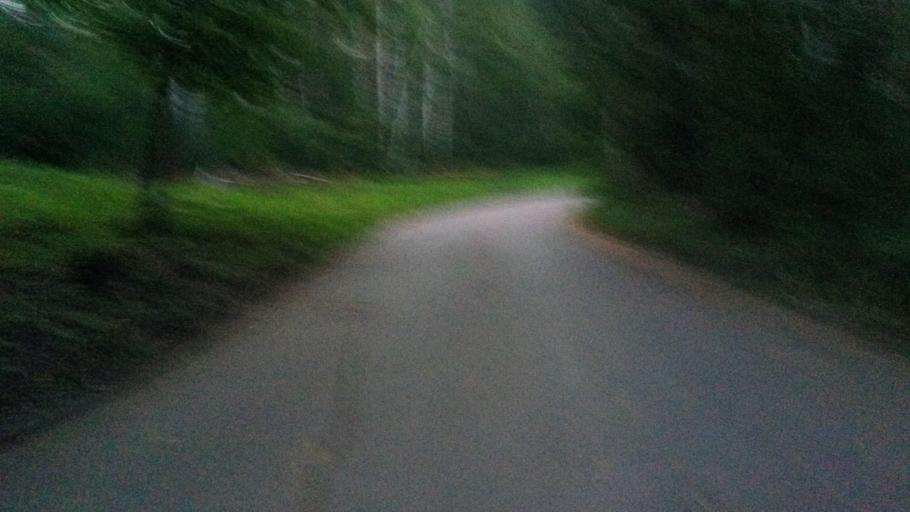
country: RU
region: Chelyabinsk
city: Turgoyak
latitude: 55.1524
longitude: 60.1614
